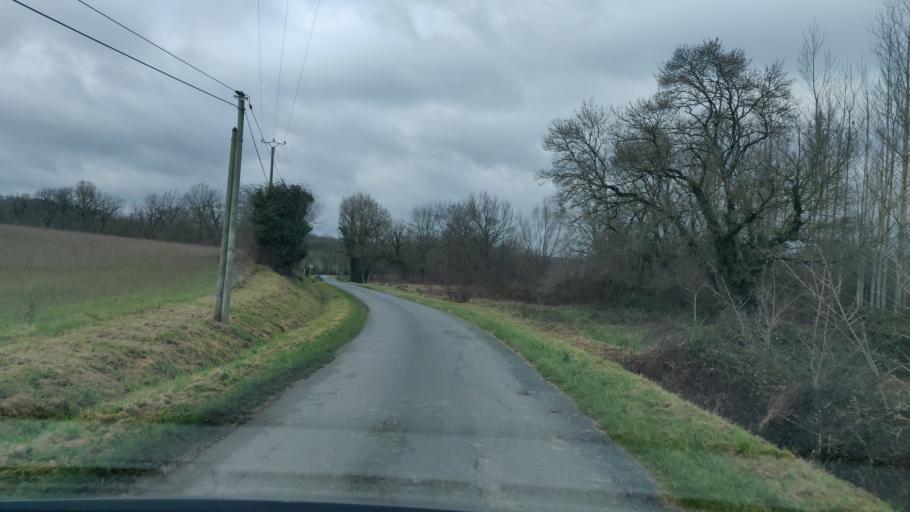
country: FR
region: Aquitaine
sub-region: Departement du Lot-et-Garonne
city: Saint-Hilaire
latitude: 44.5791
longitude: 0.7111
